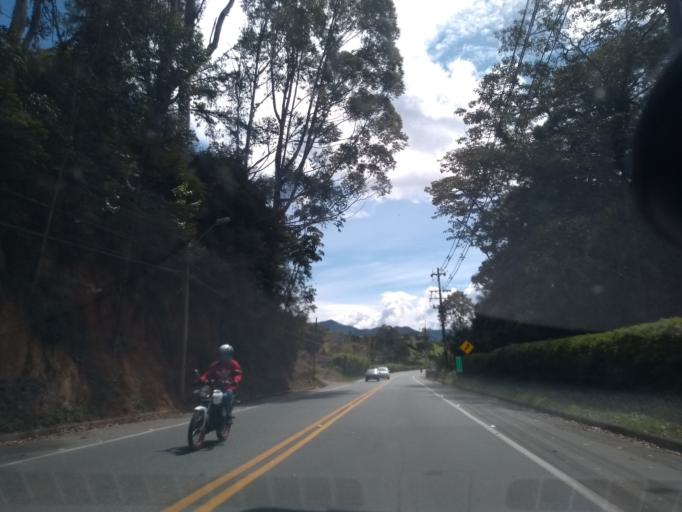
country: CO
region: Antioquia
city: Carmen de Viboral
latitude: 6.1007
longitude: -75.3836
